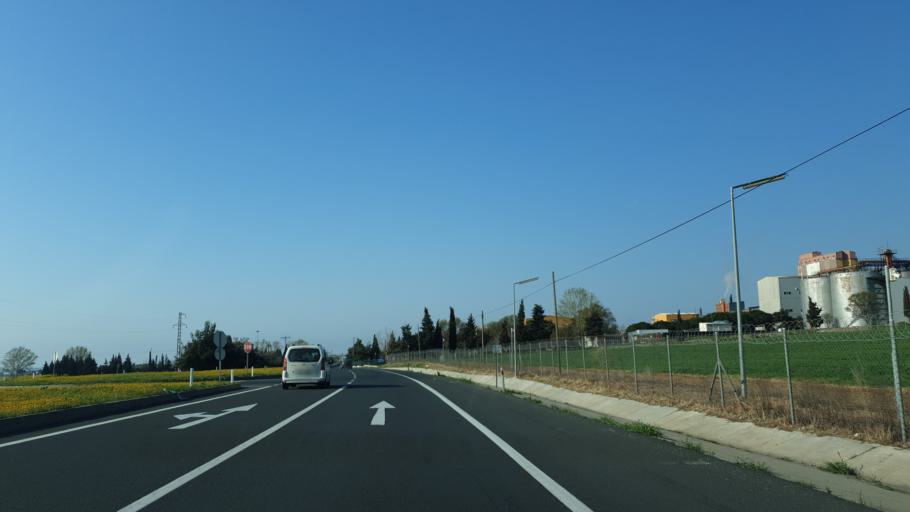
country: TR
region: Tekirdag
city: Corlu
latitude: 41.0241
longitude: 27.7235
